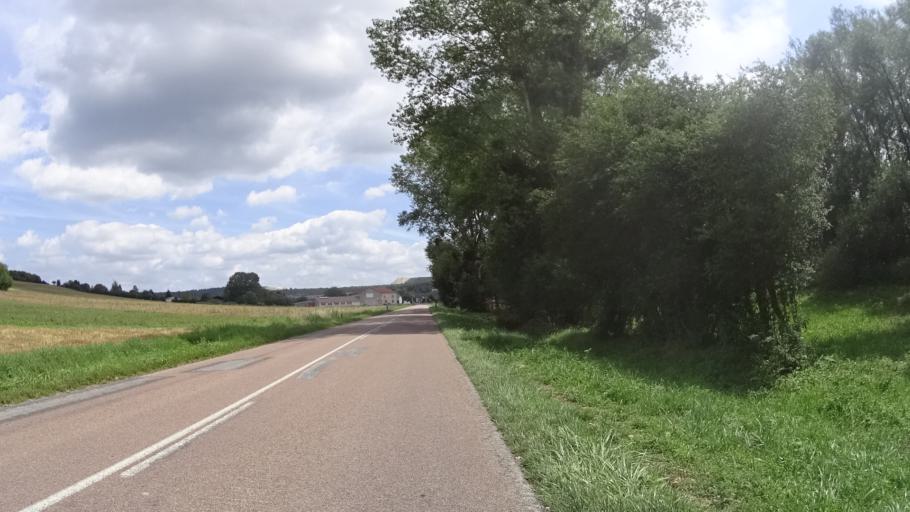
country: FR
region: Lorraine
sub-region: Departement de la Meuse
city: Euville
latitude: 48.7392
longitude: 5.6552
